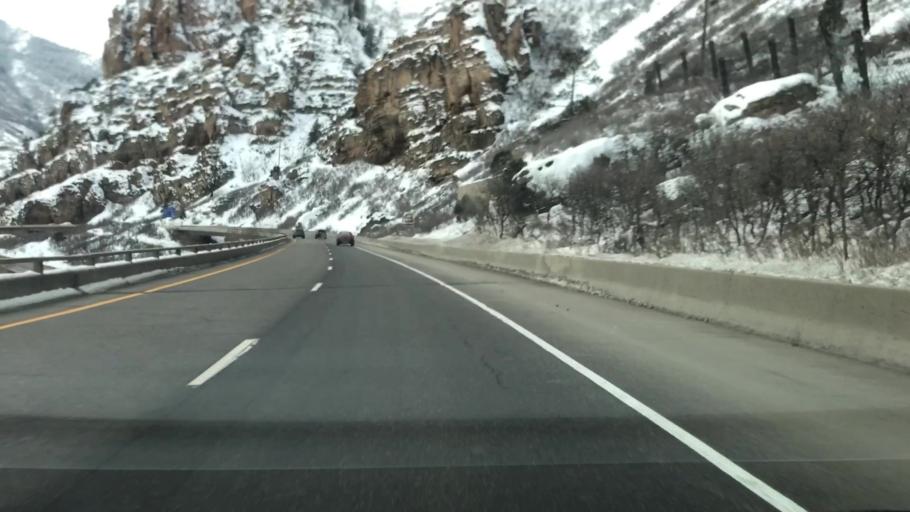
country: US
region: Colorado
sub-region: Garfield County
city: Glenwood Springs
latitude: 39.5667
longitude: -107.2736
